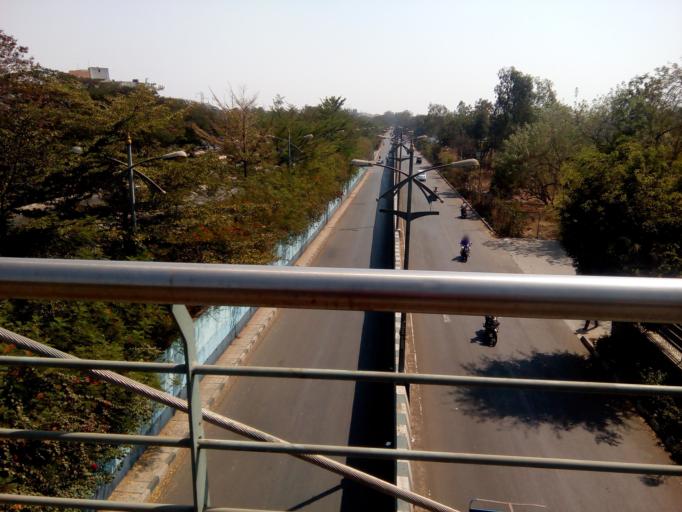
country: IN
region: Maharashtra
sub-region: Pune Division
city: Pimpri
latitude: 18.6151
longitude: 73.8152
